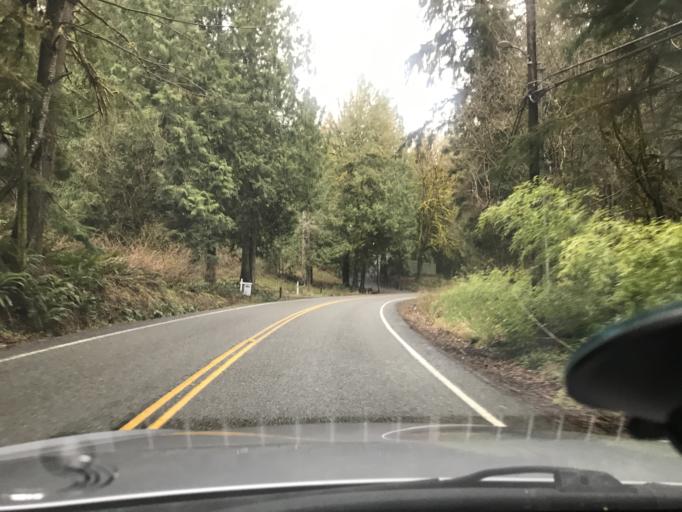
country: US
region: Washington
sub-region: King County
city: Ames Lake
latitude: 47.6484
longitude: -121.9607
